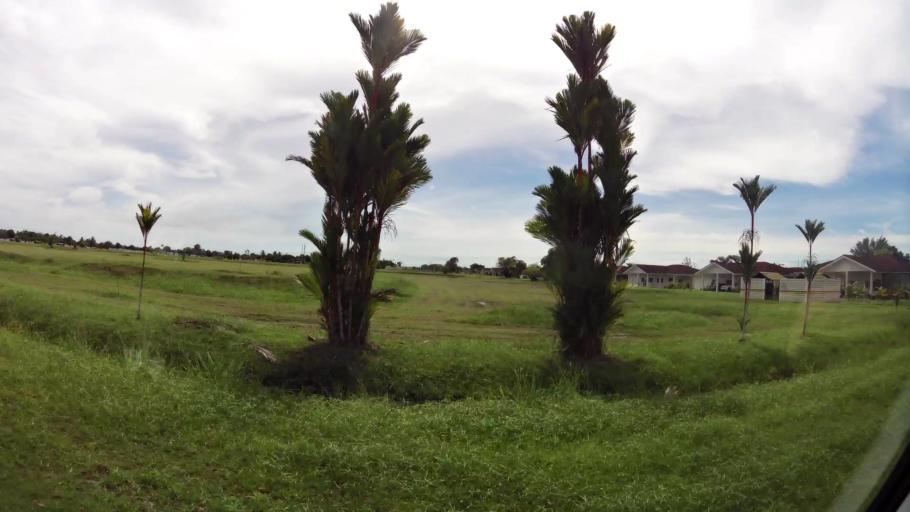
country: BN
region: Belait
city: Seria
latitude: 4.6046
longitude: 114.3172
